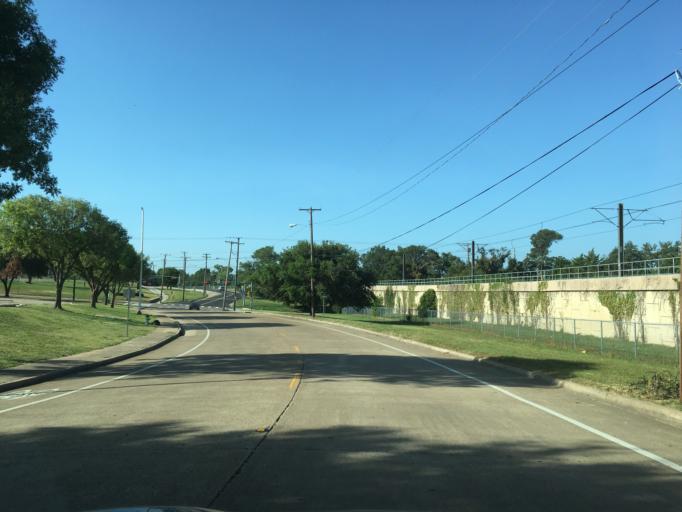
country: US
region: Texas
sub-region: Dallas County
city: Richardson
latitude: 32.8899
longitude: -96.7280
